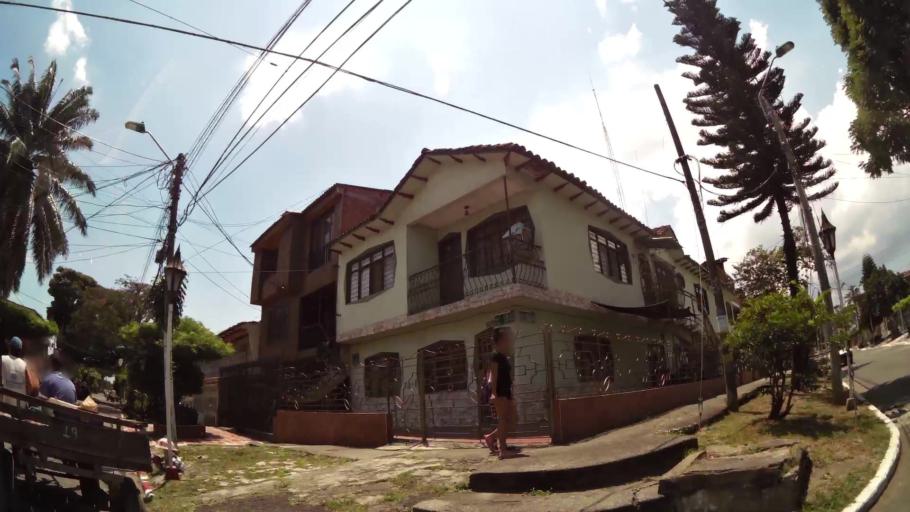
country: CO
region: Valle del Cauca
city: Cali
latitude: 3.4474
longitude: -76.4974
